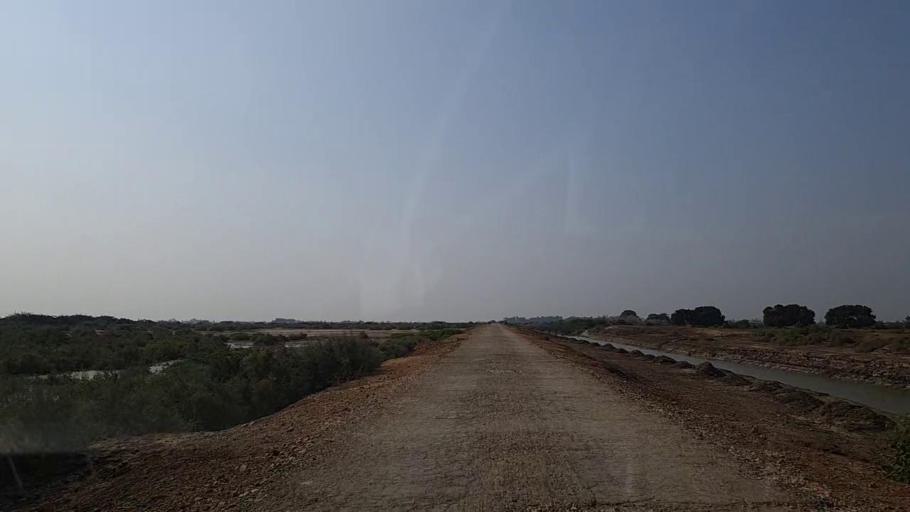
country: PK
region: Sindh
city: Mirpur Sakro
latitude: 24.6347
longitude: 67.7099
